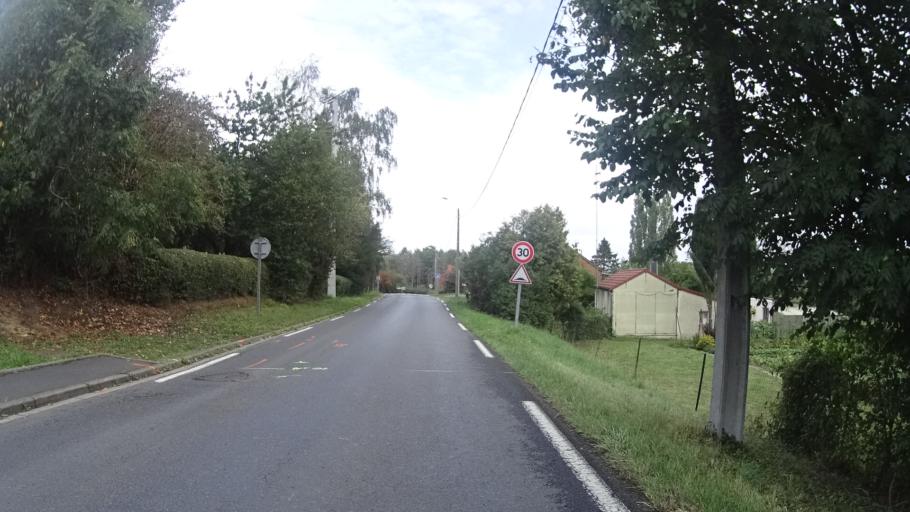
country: FR
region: Nord-Pas-de-Calais
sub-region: Departement du Nord
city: Berlaimont
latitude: 50.1916
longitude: 3.8078
